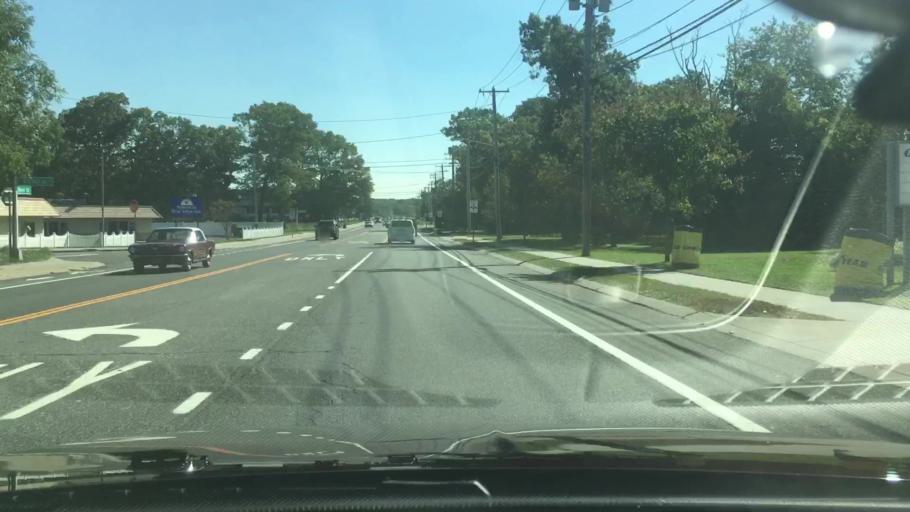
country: US
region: New York
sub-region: Suffolk County
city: Port Jefferson Station
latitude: 40.9174
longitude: -73.0367
